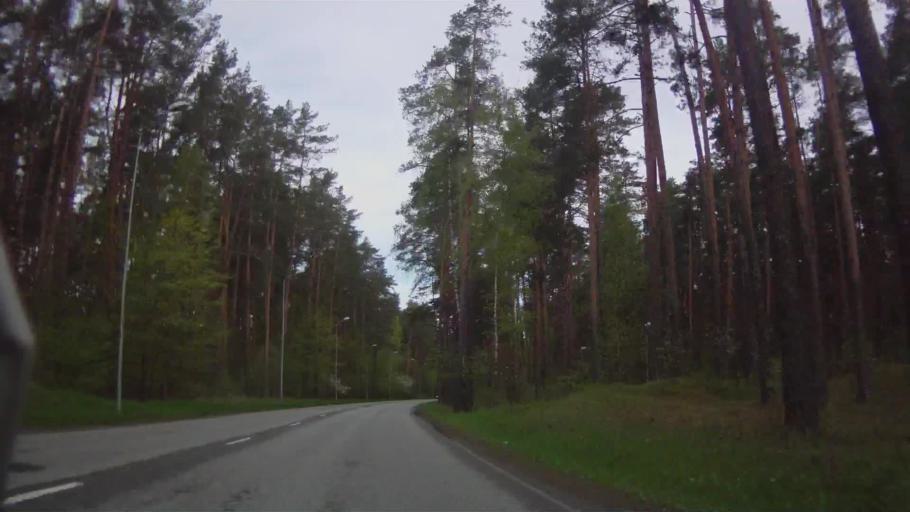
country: LV
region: Riga
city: Jaunciems
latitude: 56.9768
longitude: 24.2183
